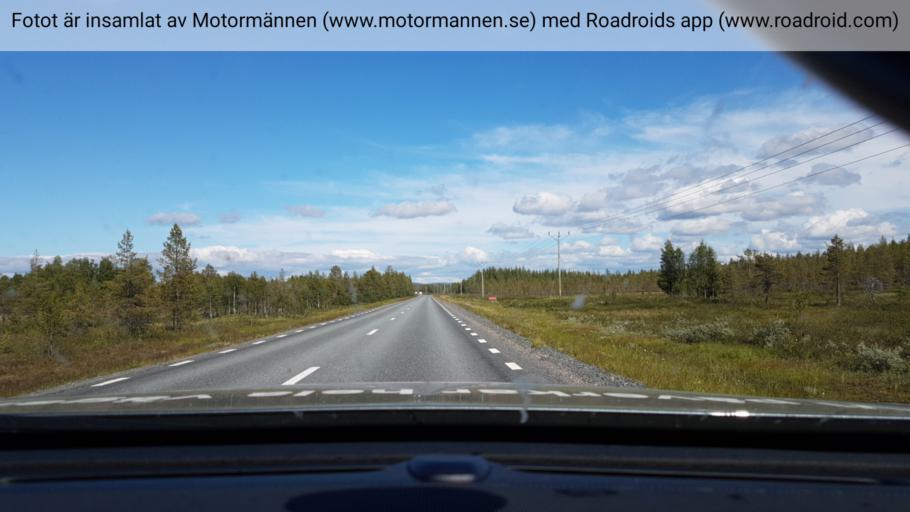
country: SE
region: Norrbotten
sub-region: Arjeplogs Kommun
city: Arjeplog
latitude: 65.5764
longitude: 18.0688
